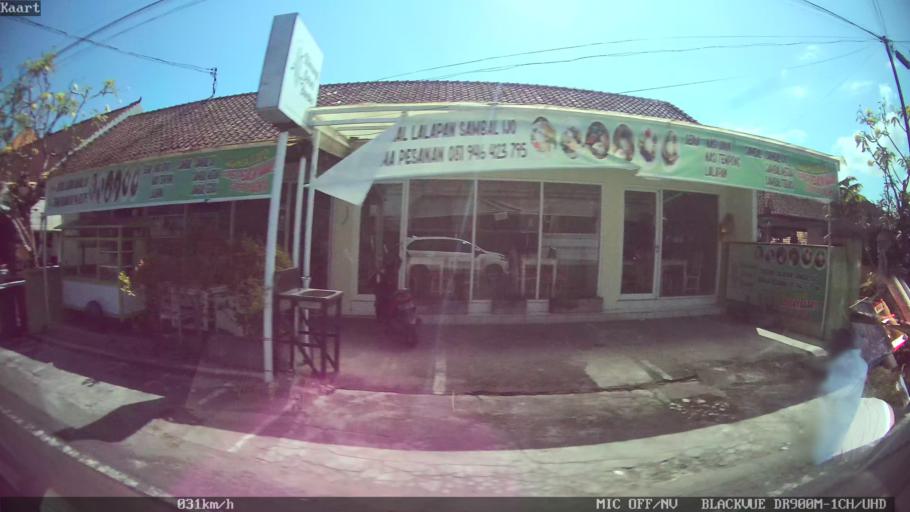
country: ID
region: Bali
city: Denpasar
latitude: -8.6676
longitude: 115.1696
